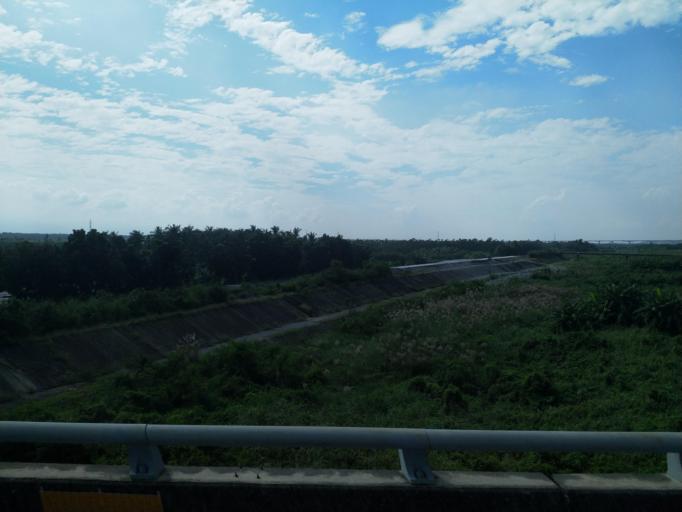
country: TW
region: Taiwan
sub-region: Pingtung
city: Pingtung
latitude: 22.7975
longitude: 120.4668
